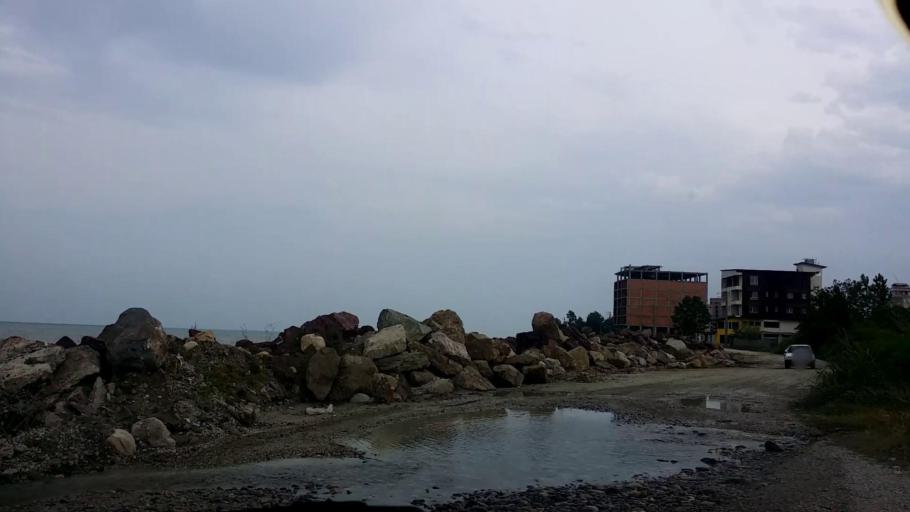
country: IR
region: Mazandaran
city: Chalus
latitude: 36.6852
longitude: 51.4281
